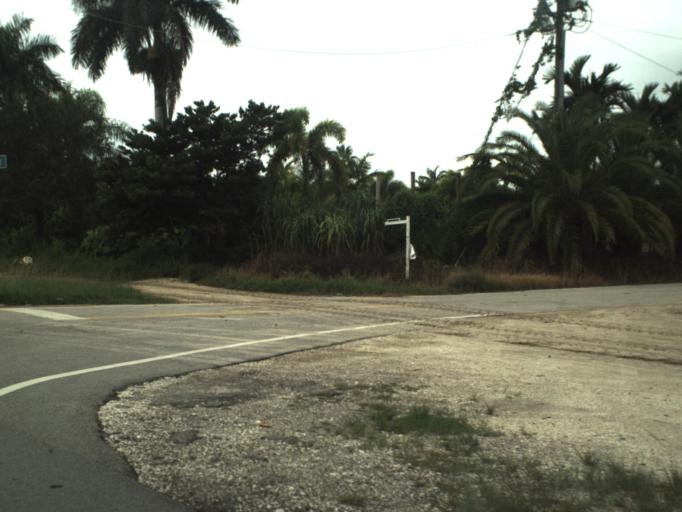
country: US
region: Florida
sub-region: Miami-Dade County
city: The Hammocks
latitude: 25.6507
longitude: -80.4805
